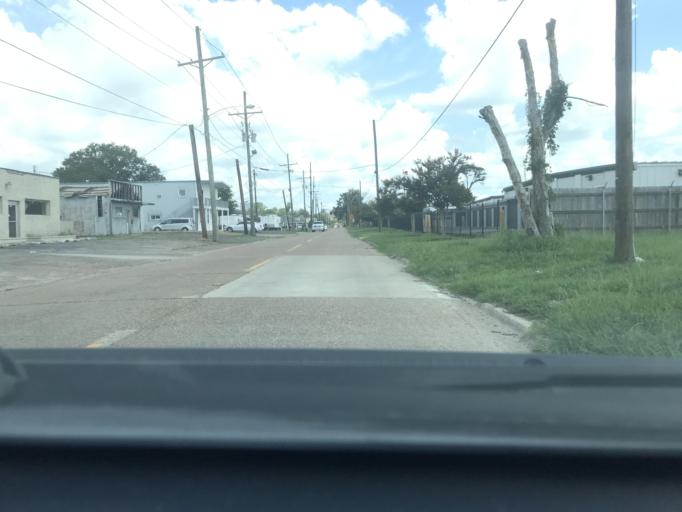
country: US
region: Louisiana
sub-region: Calcasieu Parish
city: Lake Charles
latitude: 30.2116
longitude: -93.2160
